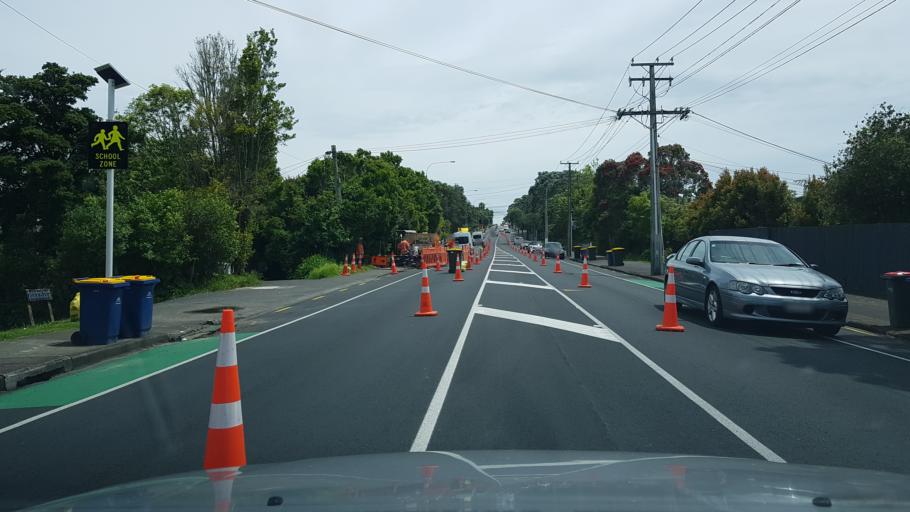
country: NZ
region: Auckland
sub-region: Auckland
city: North Shore
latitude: -36.8037
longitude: 174.7880
